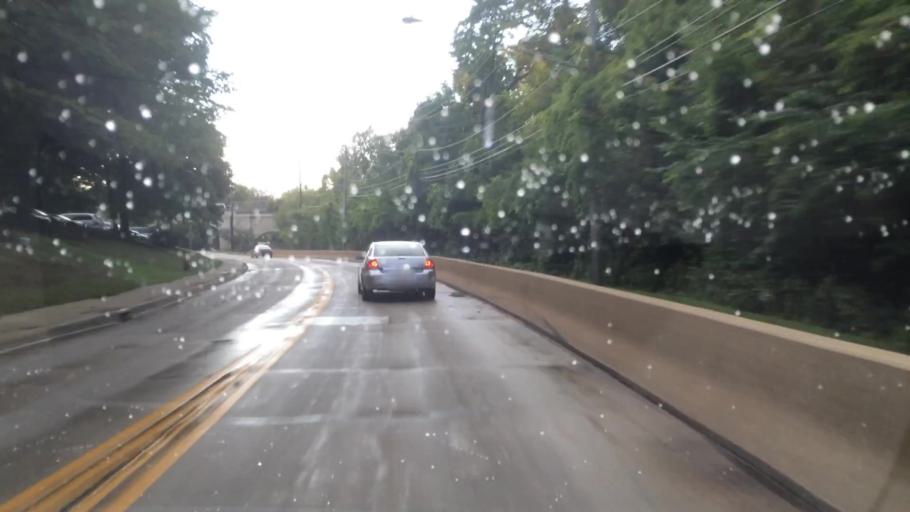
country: US
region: Ohio
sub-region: Cuyahoga County
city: Berea
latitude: 41.3747
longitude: -81.8641
